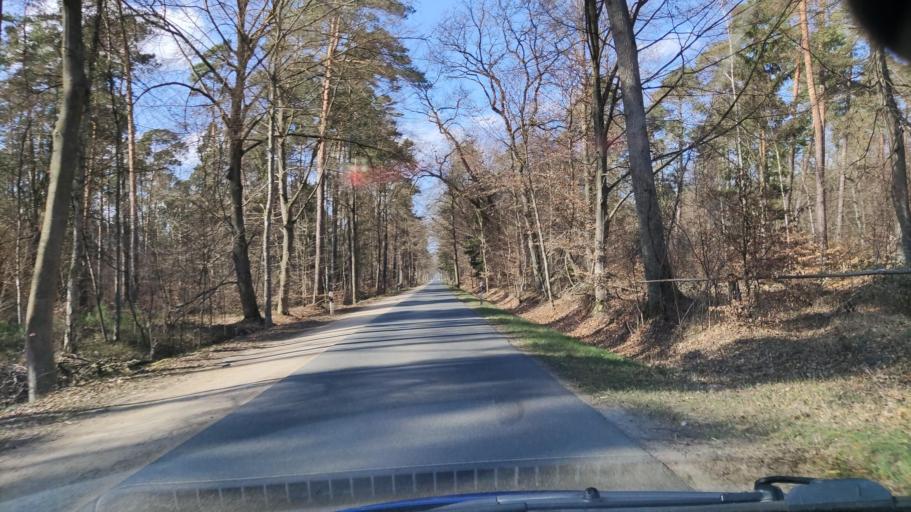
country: DE
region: Lower Saxony
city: Langendorf
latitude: 53.0438
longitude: 11.2443
